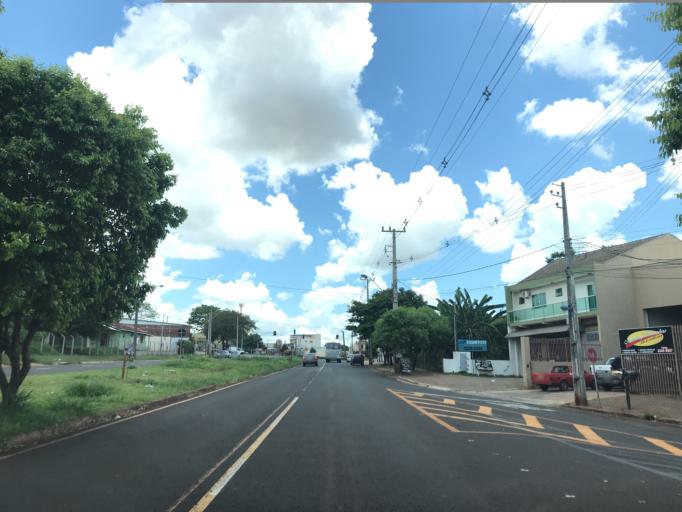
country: BR
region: Parana
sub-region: Maringa
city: Maringa
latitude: -23.3890
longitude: -51.9147
